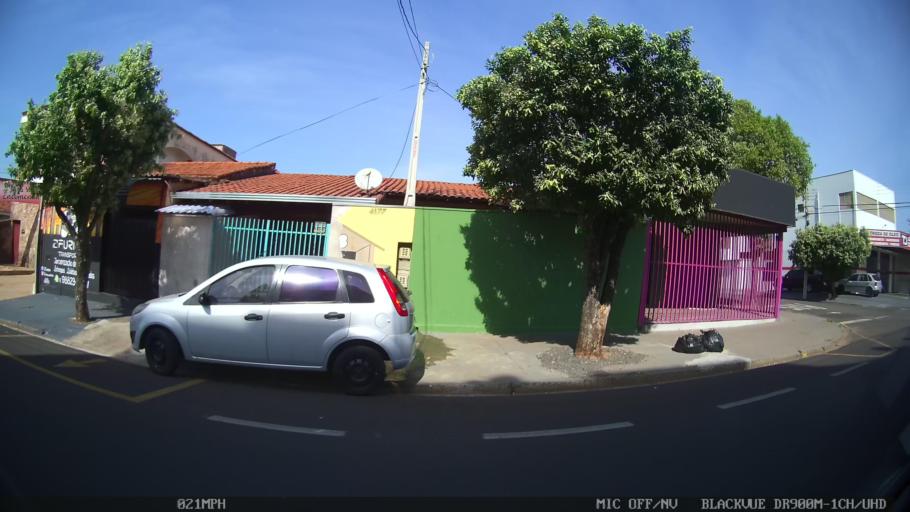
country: BR
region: Sao Paulo
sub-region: Sao Jose Do Rio Preto
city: Sao Jose do Rio Preto
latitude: -20.7953
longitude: -49.4088
